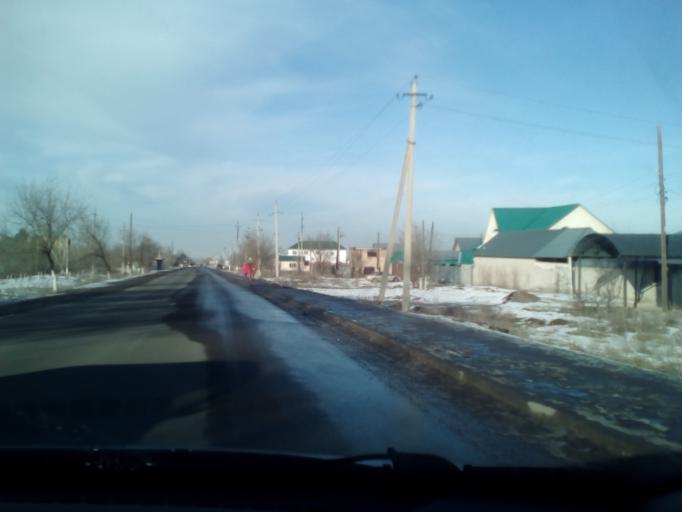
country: KZ
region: Almaty Oblysy
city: Burunday
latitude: 43.1868
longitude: 76.4148
